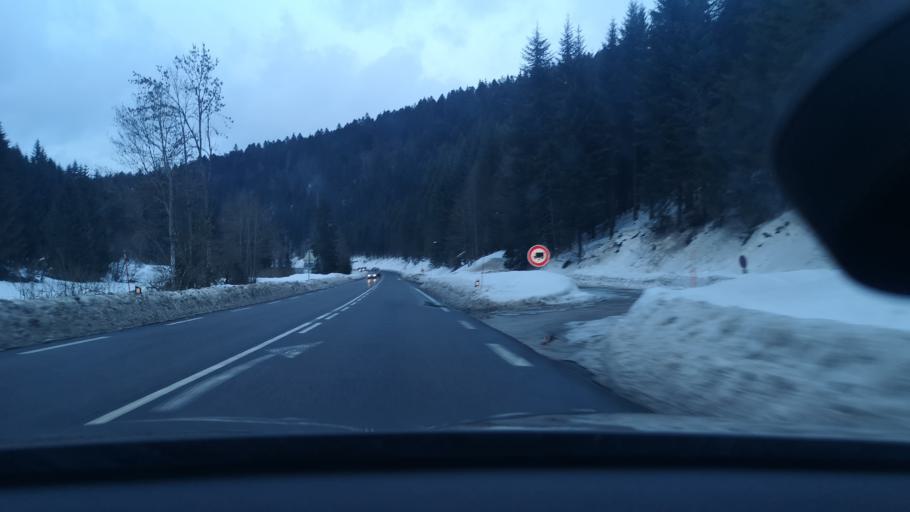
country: FR
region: Franche-Comte
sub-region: Departement du Doubs
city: Les Fourgs
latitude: 46.8159
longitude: 6.3676
